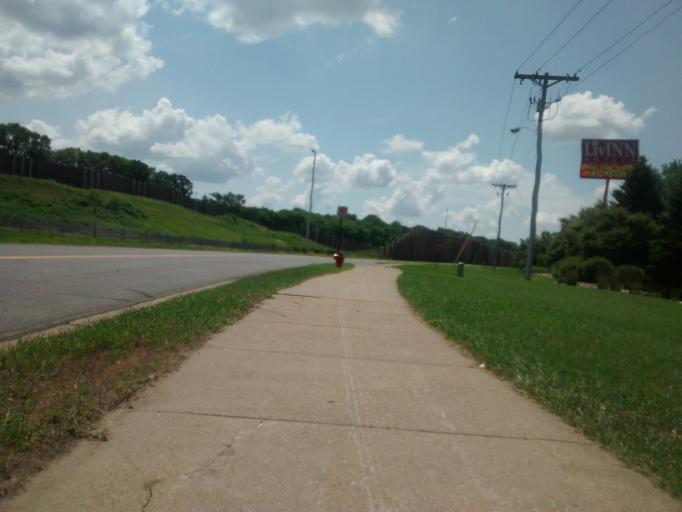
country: US
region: Minnesota
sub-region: Dakota County
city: Burnsville
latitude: 44.7675
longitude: -93.2896
